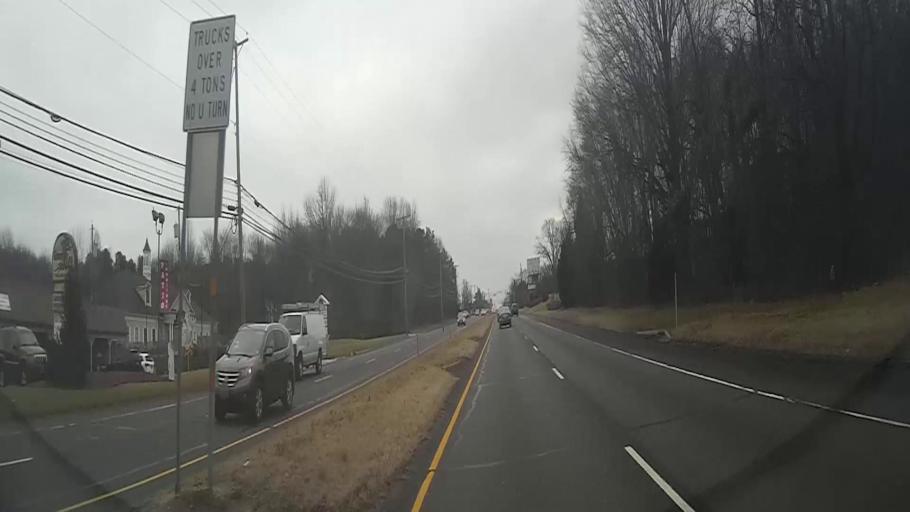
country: US
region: New Jersey
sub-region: Camden County
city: Gibbsboro
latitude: 39.8435
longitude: -74.9241
